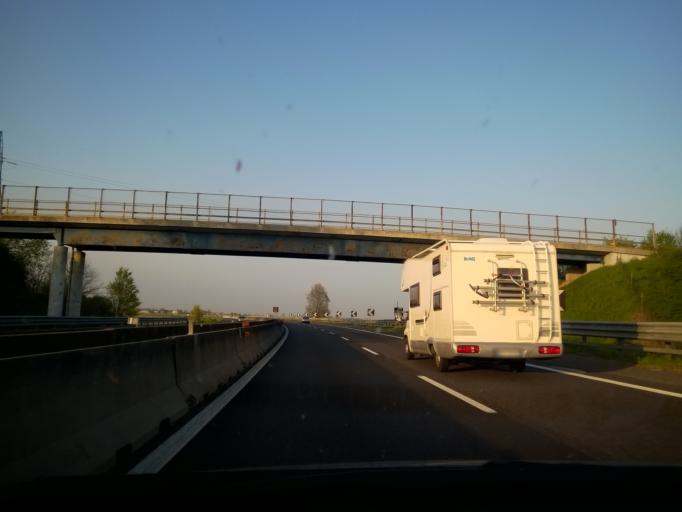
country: IT
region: Veneto
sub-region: Provincia di Rovigo
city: Fiesso Umbertiano
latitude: 44.9473
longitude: 11.6345
